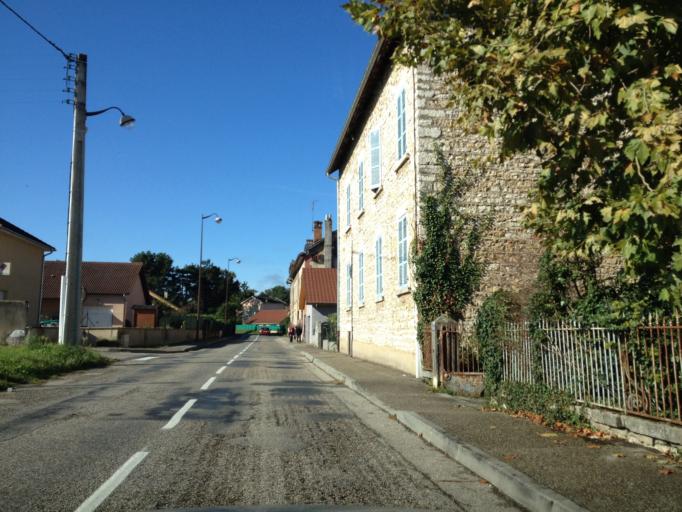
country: FR
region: Rhone-Alpes
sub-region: Departement de l'Isere
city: Morestel
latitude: 45.6713
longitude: 5.4697
